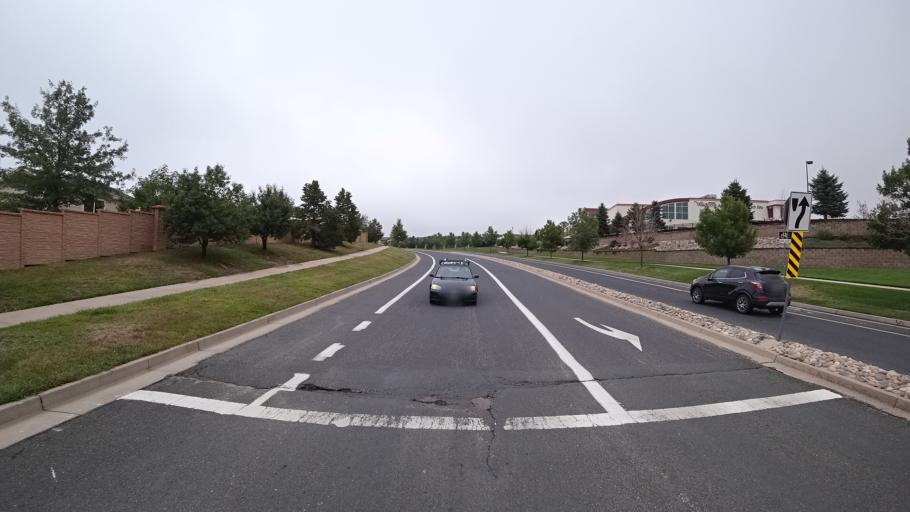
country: US
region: Colorado
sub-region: El Paso County
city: Cimarron Hills
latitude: 38.9350
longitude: -104.7231
